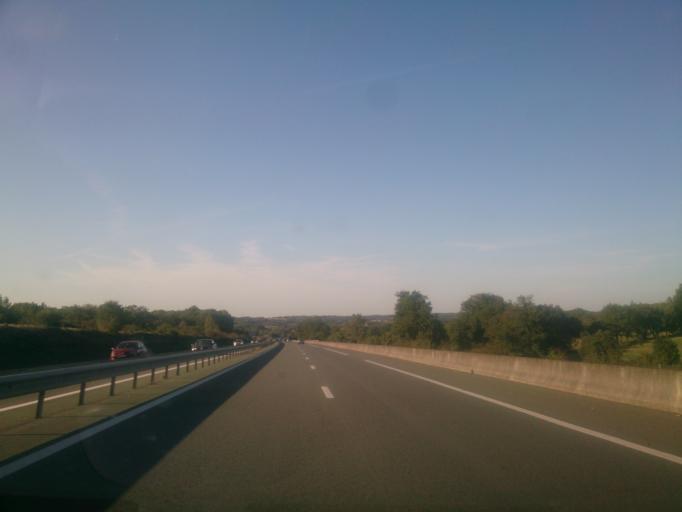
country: FR
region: Midi-Pyrenees
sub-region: Departement du Lot
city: Le Vigan
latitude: 44.6778
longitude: 1.5716
